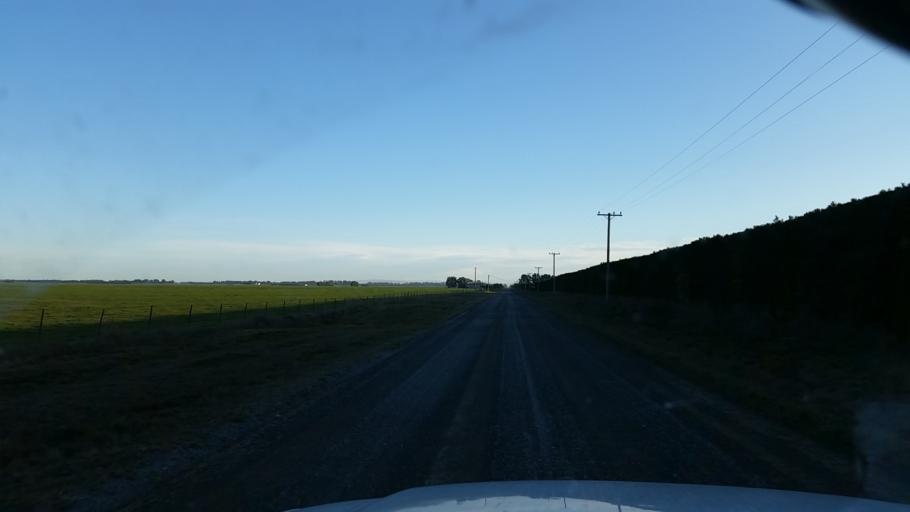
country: NZ
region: Canterbury
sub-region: Ashburton District
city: Tinwald
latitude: -43.9022
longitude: 171.6427
